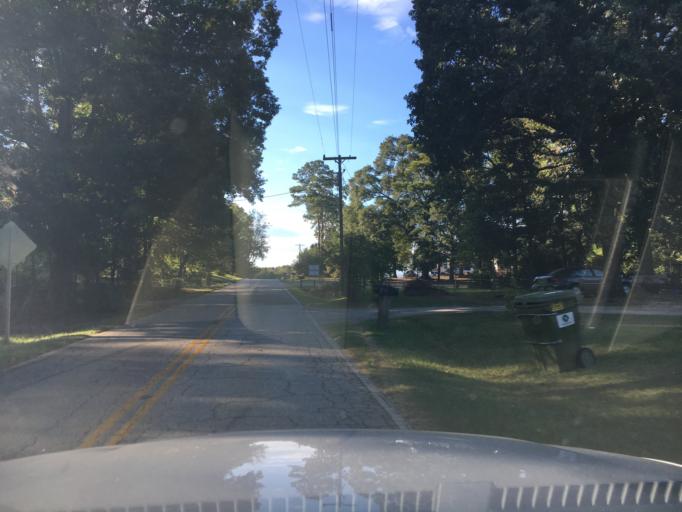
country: US
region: South Carolina
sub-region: Spartanburg County
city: Woodruff
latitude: 34.8222
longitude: -82.0985
